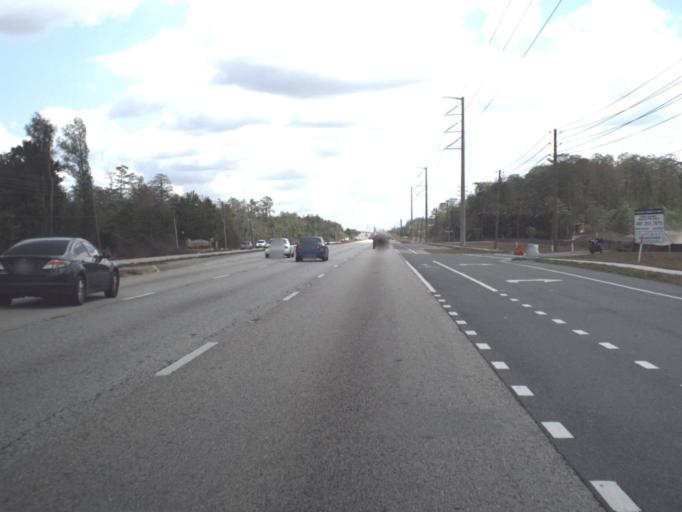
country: US
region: Florida
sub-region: Orange County
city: Sky Lake
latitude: 28.4508
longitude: -81.3820
